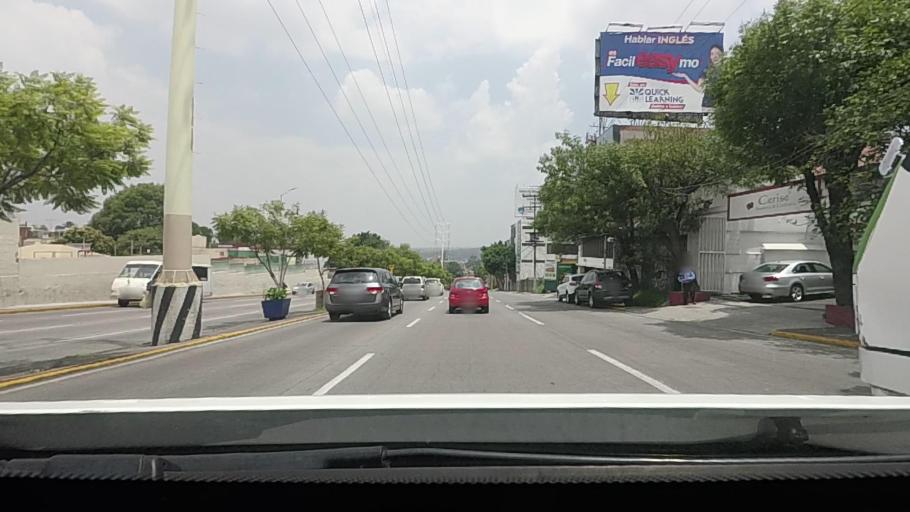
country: MX
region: Mexico
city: Naucalpan de Juarez
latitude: 19.5002
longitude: -99.2498
